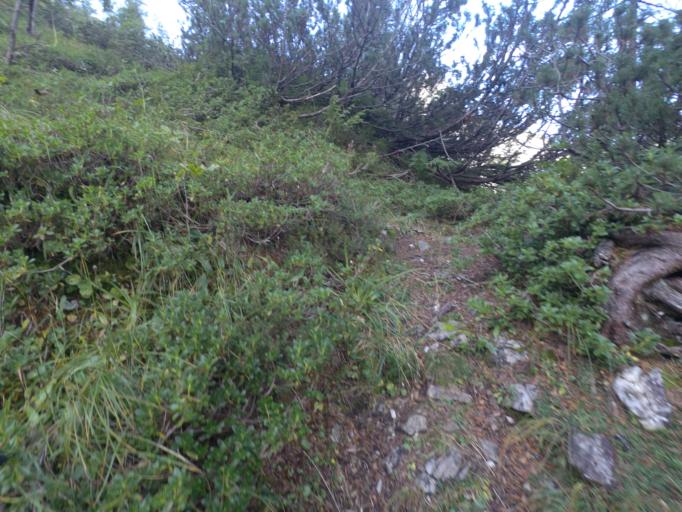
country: AT
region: Salzburg
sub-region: Politischer Bezirk Sankt Johann im Pongau
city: Untertauern
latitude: 47.2294
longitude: 13.4265
